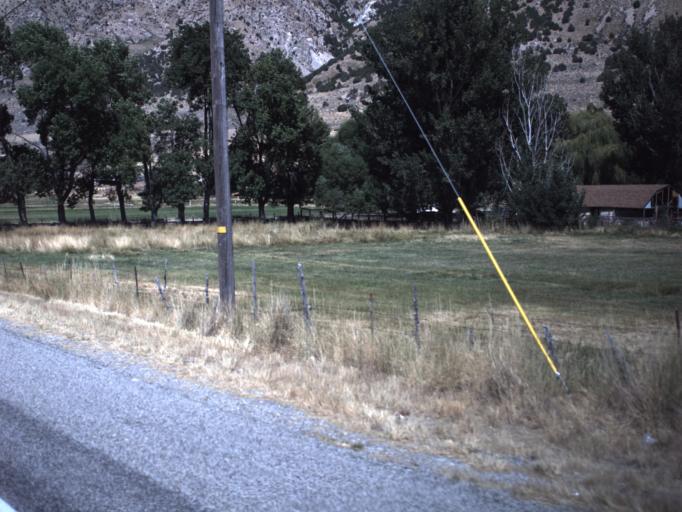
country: US
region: Utah
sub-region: Box Elder County
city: Brigham City
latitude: 41.5349
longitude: -112.0154
